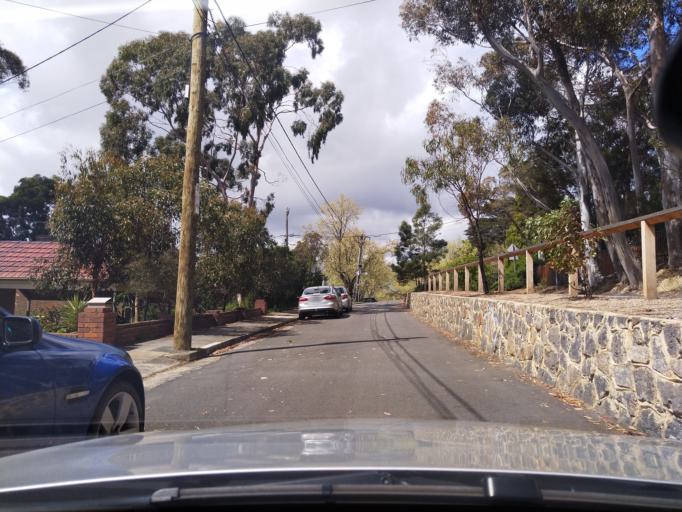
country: AU
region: Victoria
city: Rosanna
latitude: -37.7595
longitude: 145.0592
